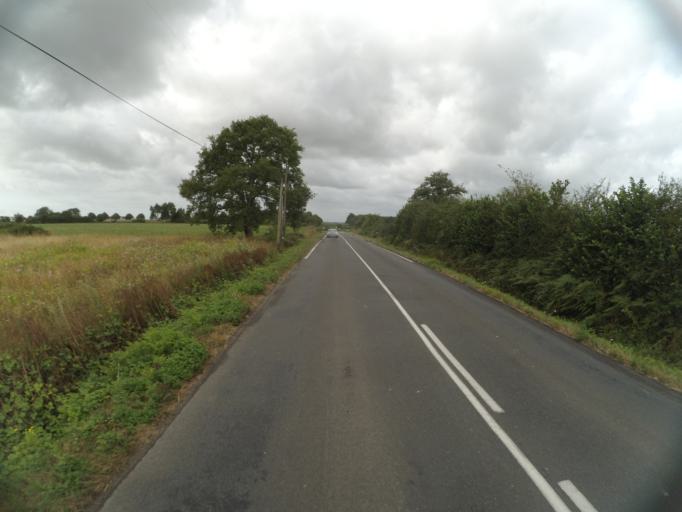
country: FR
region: Pays de la Loire
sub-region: Departement de Maine-et-Loire
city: Saint-Germain-sur-Moine
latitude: 47.1233
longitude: -1.0937
